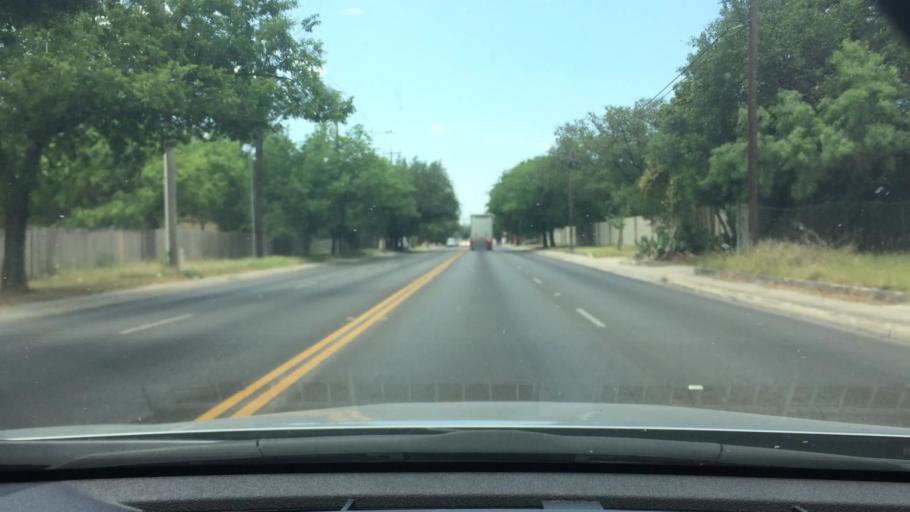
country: US
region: Texas
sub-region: Bexar County
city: Hollywood Park
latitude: 29.5714
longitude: -98.4489
